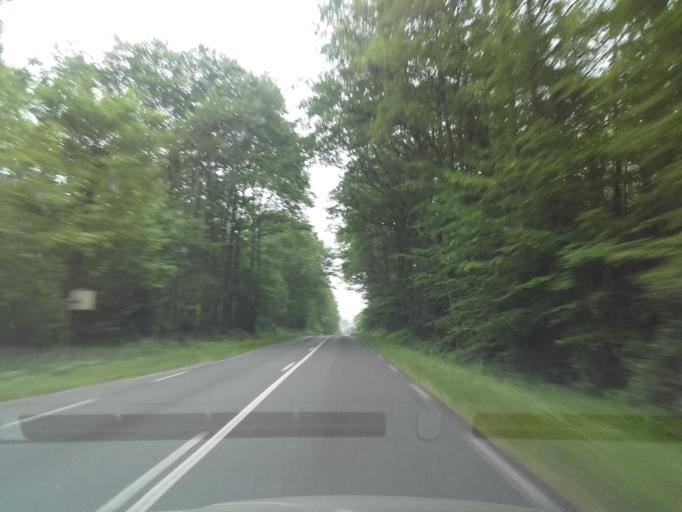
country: FR
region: Centre
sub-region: Departement d'Indre-et-Loire
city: Cerelles
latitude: 47.5020
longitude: 0.6969
